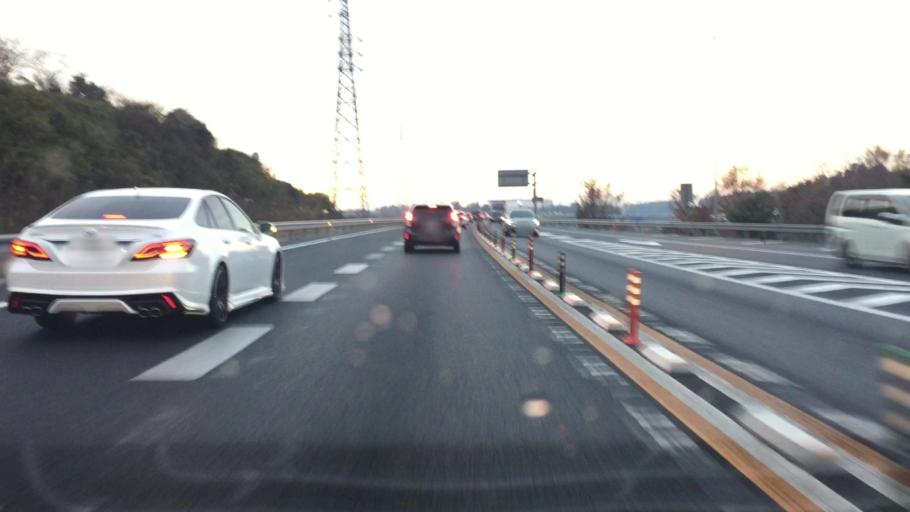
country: JP
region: Ibaraki
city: Ami
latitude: 35.9812
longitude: 140.2379
